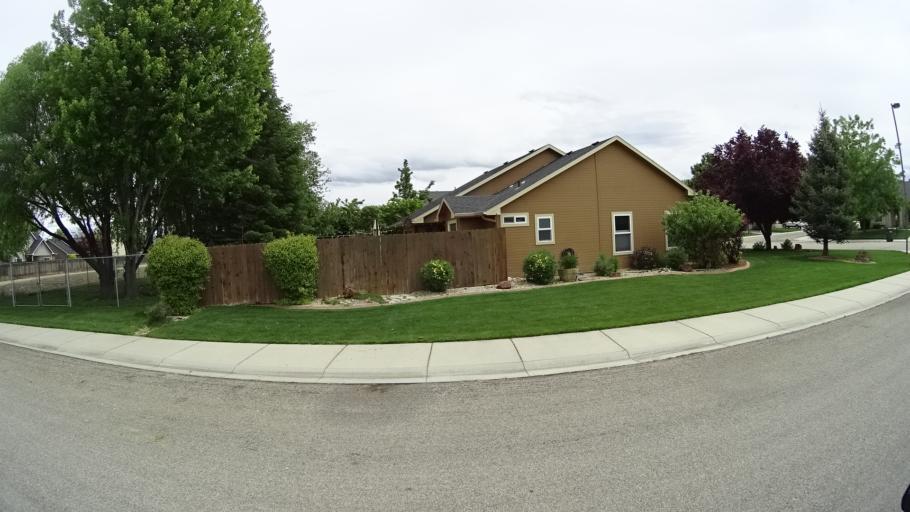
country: US
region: Idaho
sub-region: Ada County
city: Meridian
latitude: 43.6408
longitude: -116.4003
